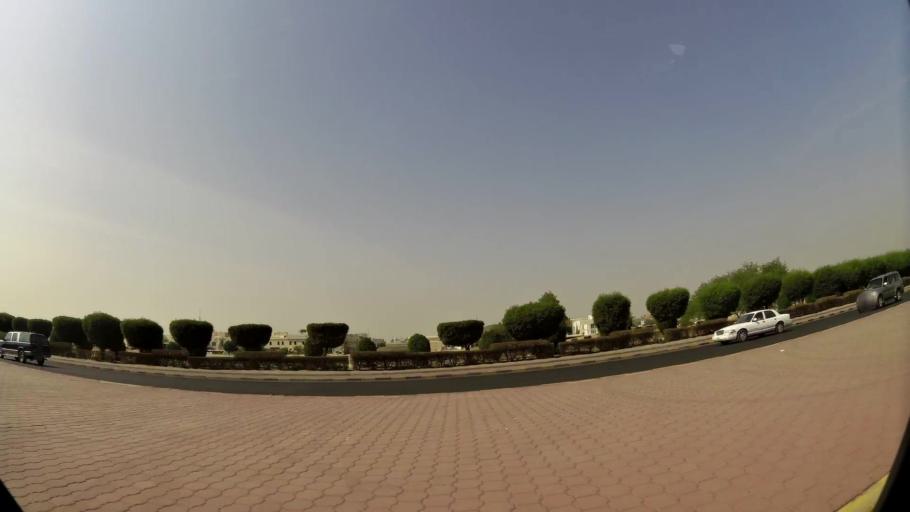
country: KW
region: Al Asimah
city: Ar Rabiyah
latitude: 29.2924
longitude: 47.9283
